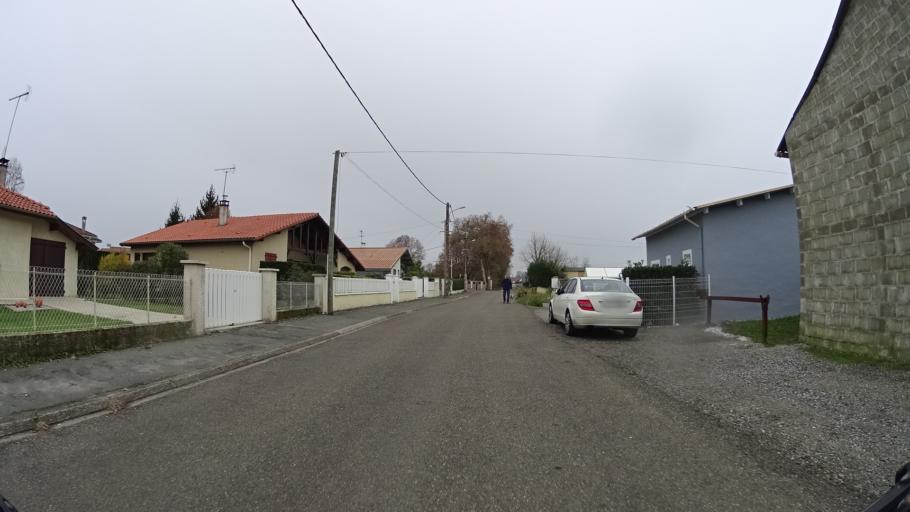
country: FR
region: Aquitaine
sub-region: Departement des Landes
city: Saint-Paul-les-Dax
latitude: 43.7329
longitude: -1.0513
